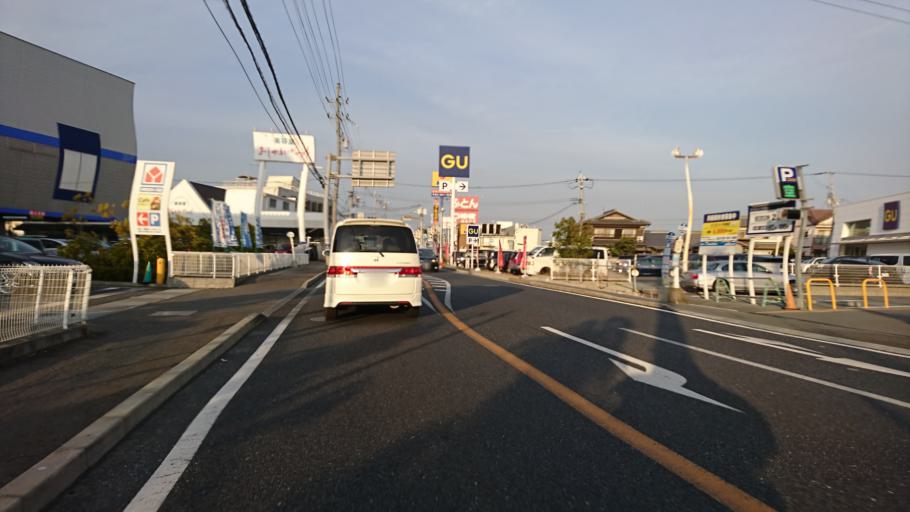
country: JP
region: Hyogo
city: Kakogawacho-honmachi
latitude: 34.7355
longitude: 134.8531
